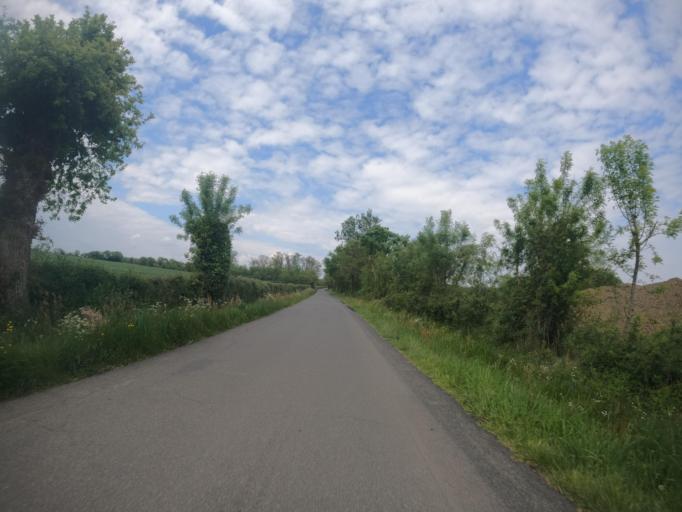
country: FR
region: Poitou-Charentes
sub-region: Departement des Deux-Sevres
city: Saint-Varent
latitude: 46.8797
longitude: -0.2948
